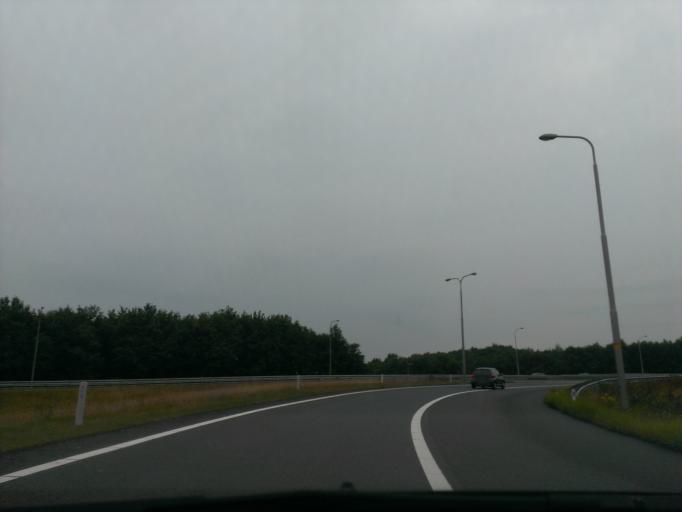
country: NL
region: Drenthe
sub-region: Gemeente Hoogeveen
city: Hoogeveen
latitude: 52.7066
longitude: 6.4581
